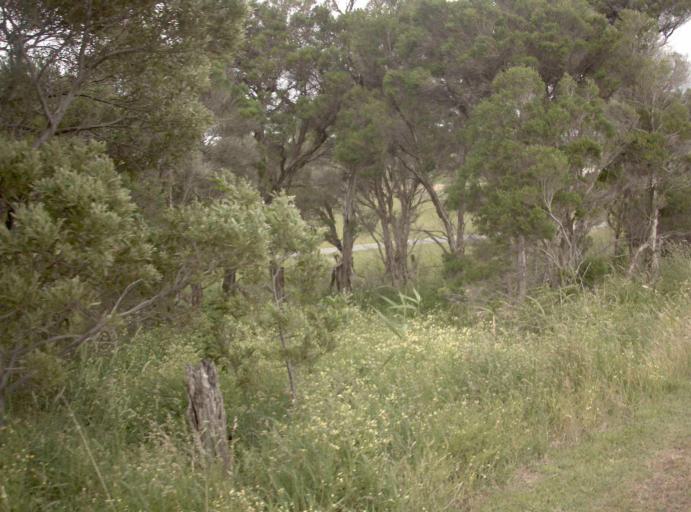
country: AU
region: Victoria
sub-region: Bass Coast
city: North Wonthaggi
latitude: -38.5545
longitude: 145.6537
